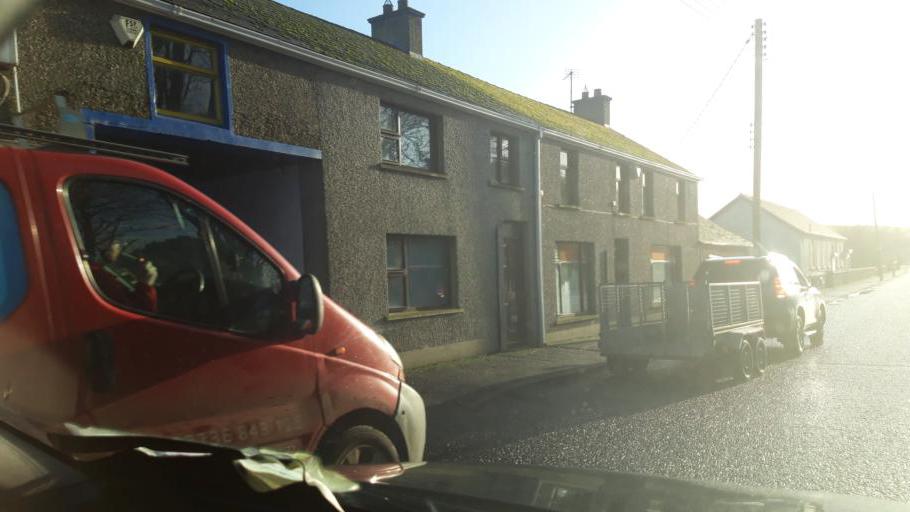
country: GB
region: Northern Ireland
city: Garvagh
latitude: 54.9810
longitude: -6.6882
